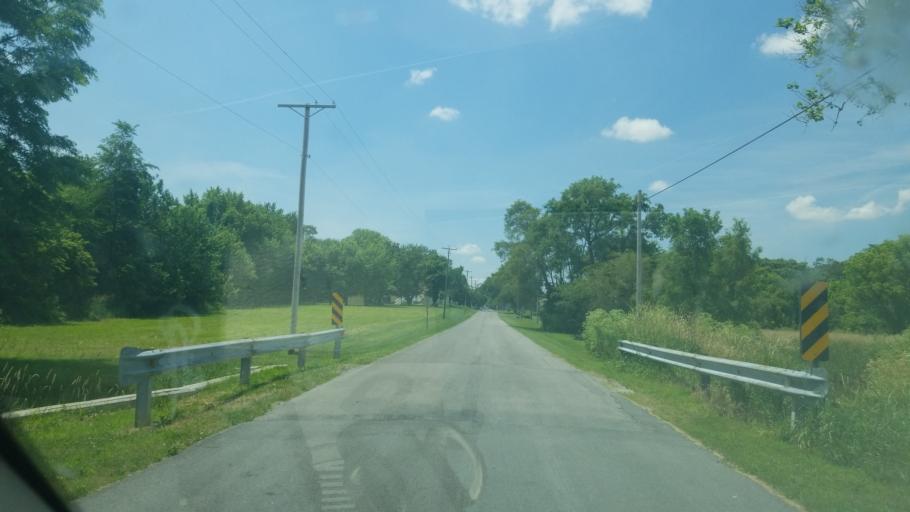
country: US
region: Ohio
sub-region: Hancock County
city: Arlington
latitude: 40.7901
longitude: -83.6345
